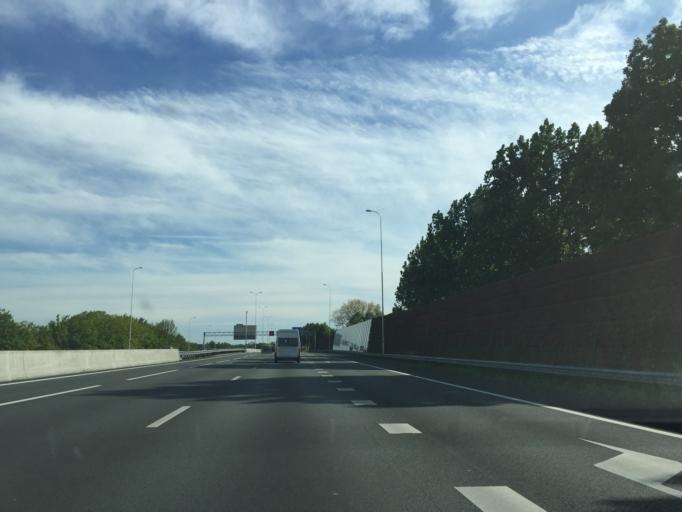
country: NL
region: Utrecht
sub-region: Gemeente Amersfoort
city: Randenbroek
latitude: 52.1622
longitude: 5.4199
